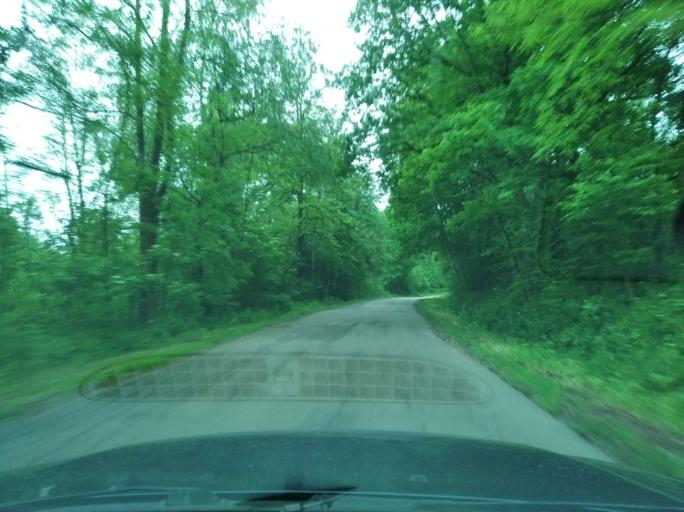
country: PL
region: Subcarpathian Voivodeship
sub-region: Powiat brzozowski
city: Orzechowka
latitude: 49.7272
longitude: 21.9317
